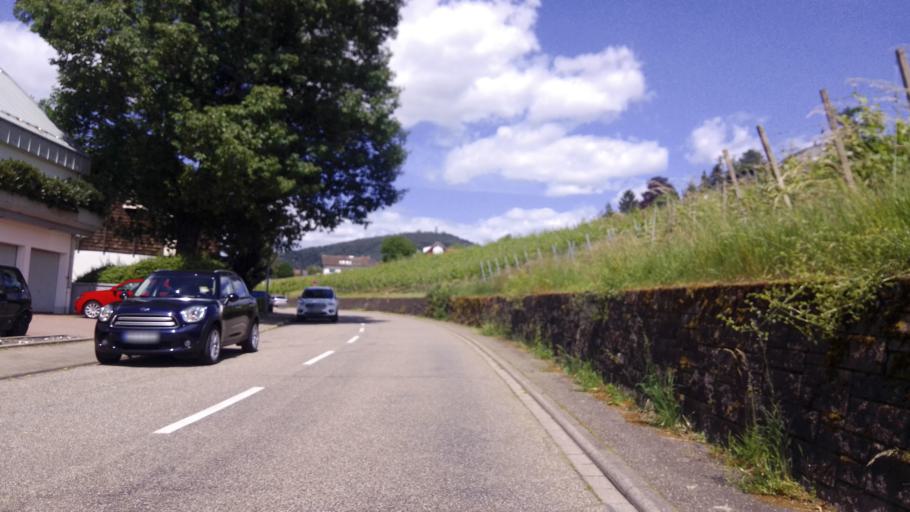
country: DE
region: Baden-Wuerttemberg
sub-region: Karlsruhe Region
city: Sinzheim
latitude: 48.7325
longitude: 8.1789
